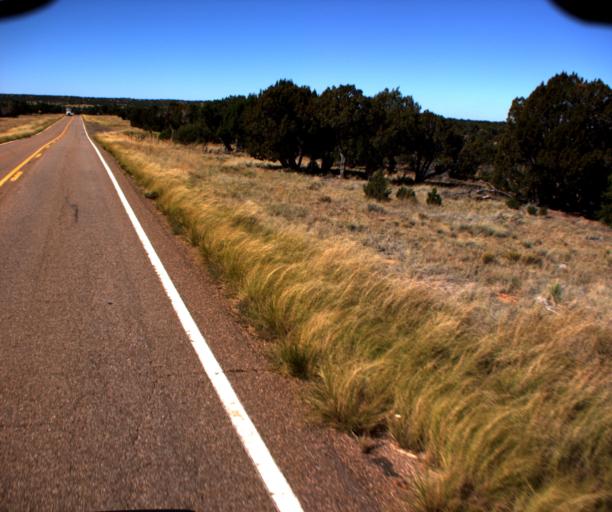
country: US
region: Arizona
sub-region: Navajo County
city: Heber-Overgaard
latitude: 34.4551
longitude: -110.4483
